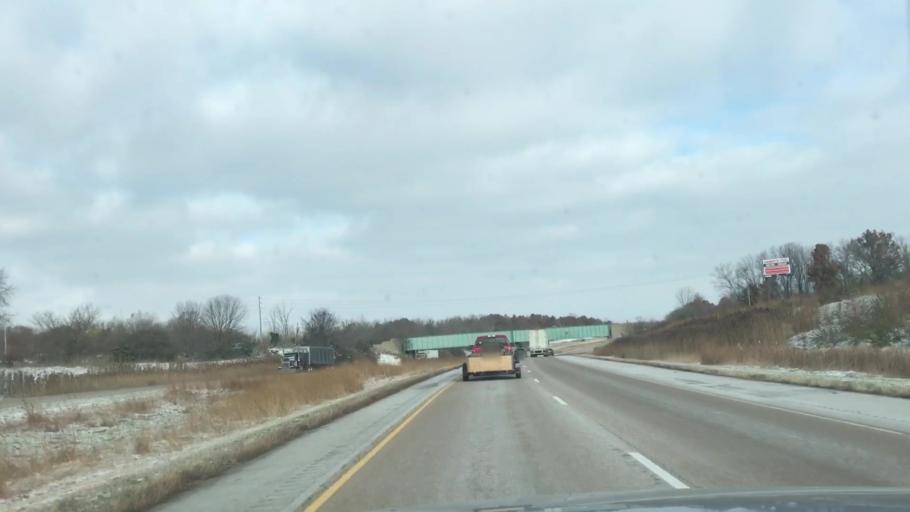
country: US
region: Illinois
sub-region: Macoupin County
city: Staunton
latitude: 39.0336
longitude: -89.7541
